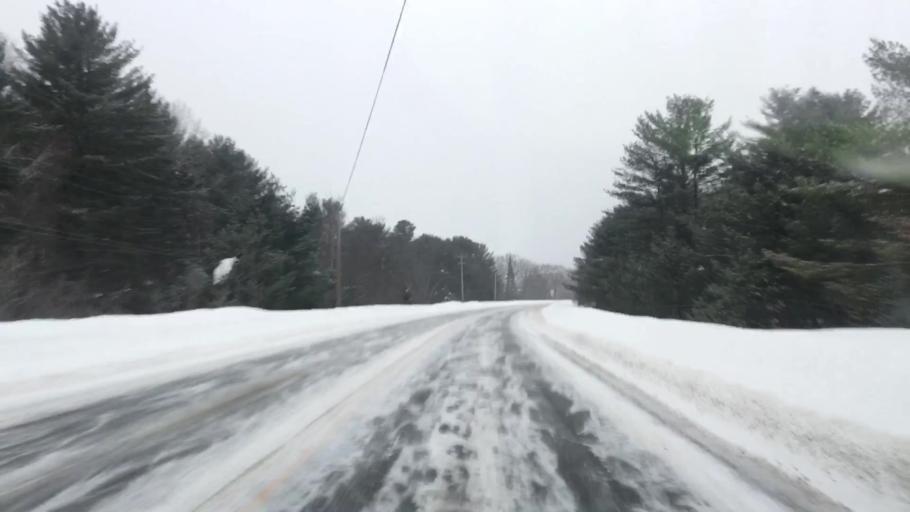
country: US
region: Maine
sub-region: Penobscot County
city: Medway
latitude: 45.5647
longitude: -68.3990
